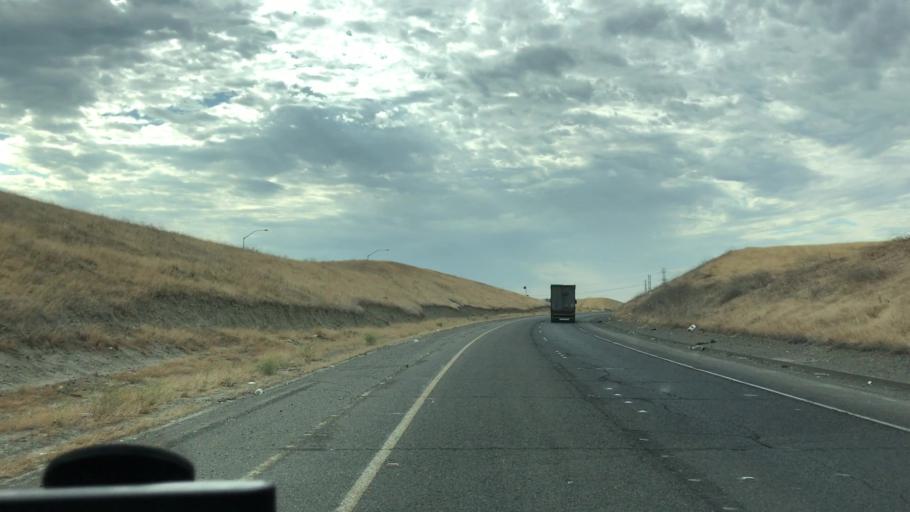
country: US
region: California
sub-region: San Joaquin County
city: Mountain House
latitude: 37.7403
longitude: -121.5600
